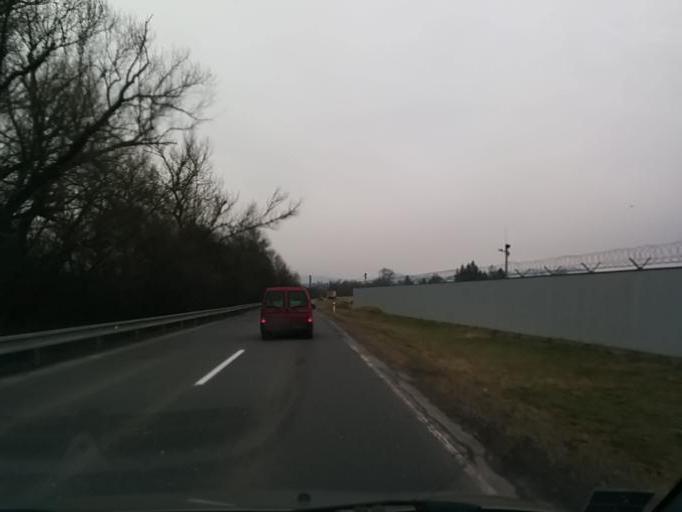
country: SK
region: Banskobystricky
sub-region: Okres Banska Bystrica
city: Zvolen
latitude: 48.6279
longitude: 19.1397
